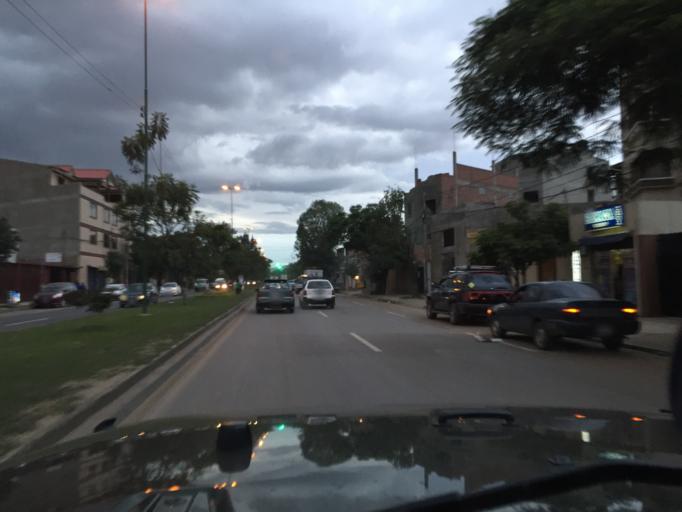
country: BO
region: Cochabamba
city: Cochabamba
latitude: -17.4016
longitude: -66.1826
